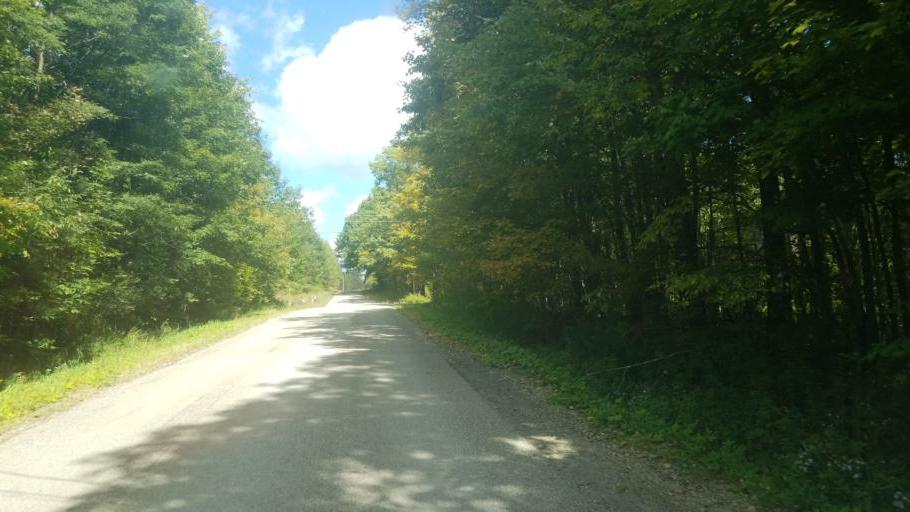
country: US
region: New York
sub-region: Allegany County
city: Cuba
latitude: 42.1973
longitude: -78.3090
